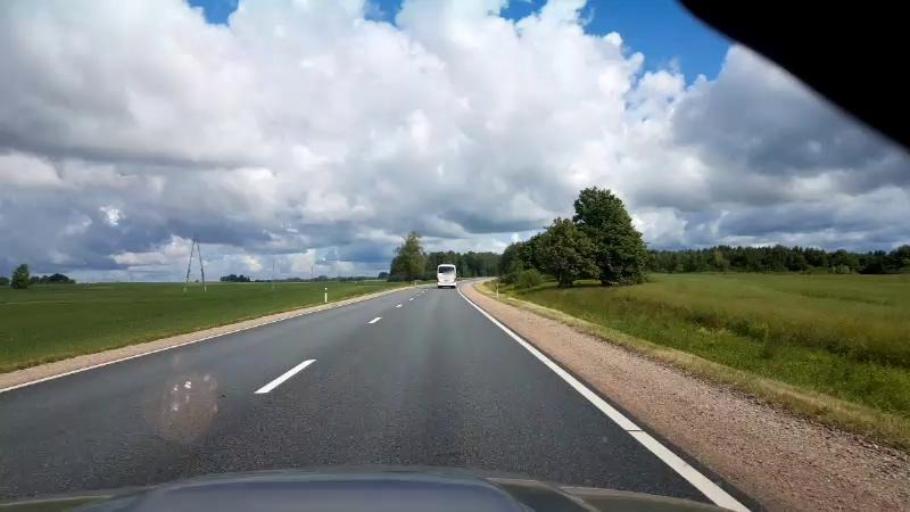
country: LV
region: Lecava
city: Iecava
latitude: 56.5108
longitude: 24.1726
